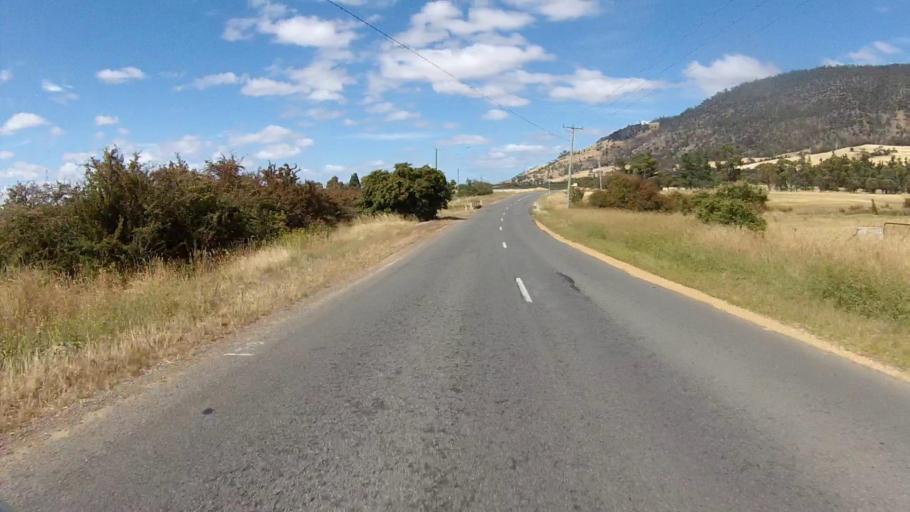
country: AU
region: Tasmania
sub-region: Sorell
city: Sorell
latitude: -42.6213
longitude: 147.4297
